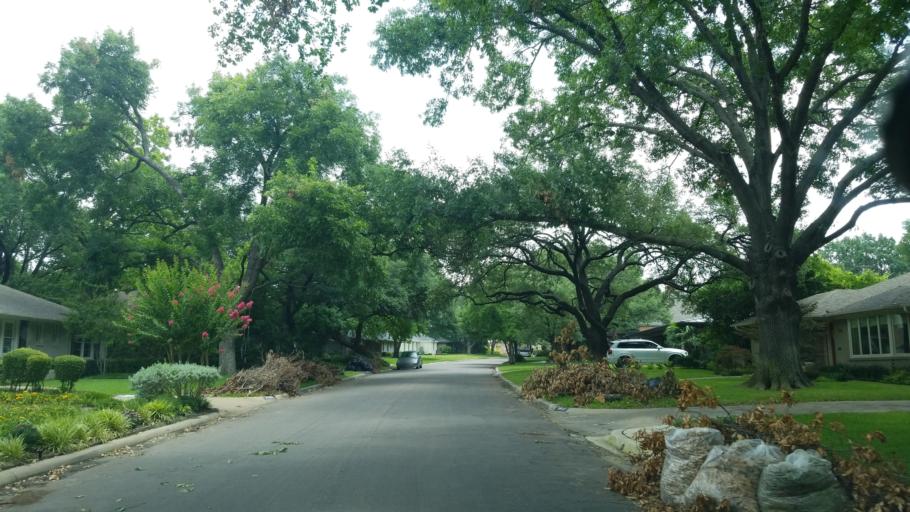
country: US
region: Texas
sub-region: Dallas County
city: University Park
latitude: 32.8329
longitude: -96.8211
